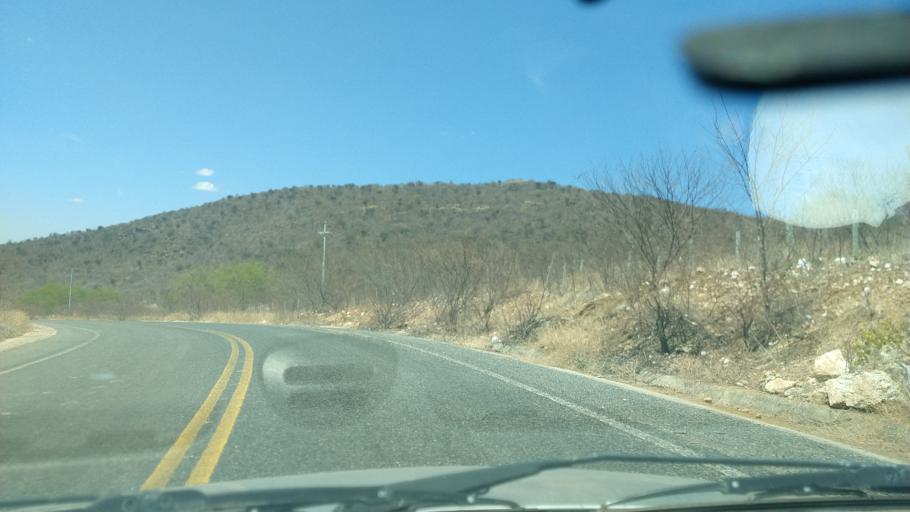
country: BR
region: Rio Grande do Norte
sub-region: Sao Tome
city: Sao Tome
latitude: -5.9669
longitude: -36.1573
